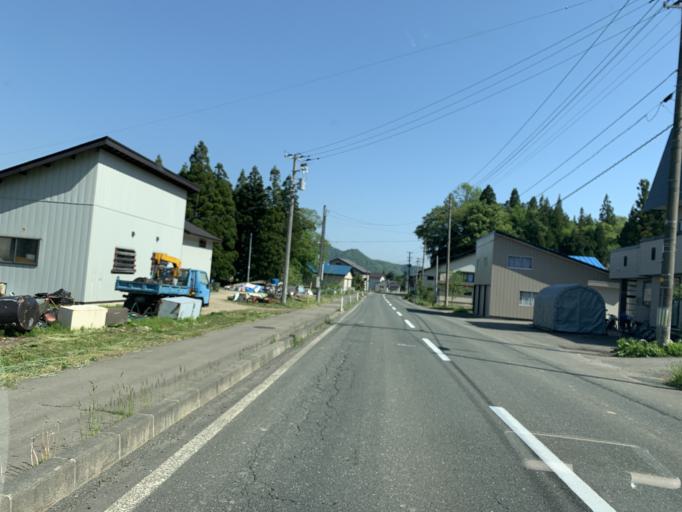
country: JP
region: Akita
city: Yokotemachi
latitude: 39.4102
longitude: 140.7499
